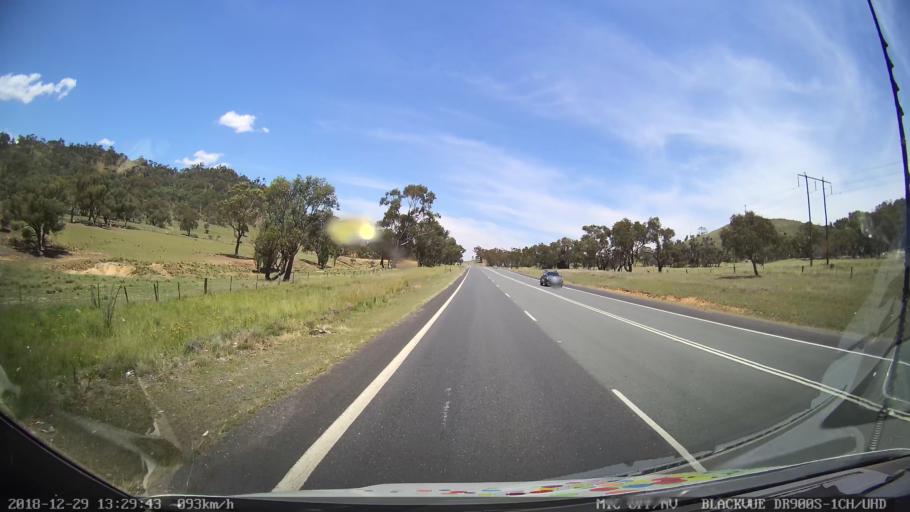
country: AU
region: New South Wales
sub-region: Cooma-Monaro
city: Cooma
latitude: -35.8940
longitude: 149.1612
